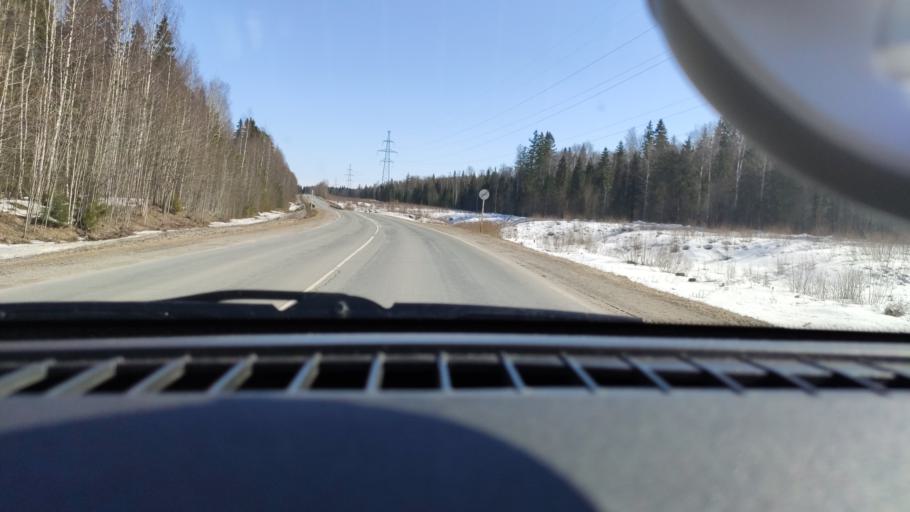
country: RU
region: Perm
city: Perm
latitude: 58.1384
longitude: 56.2746
